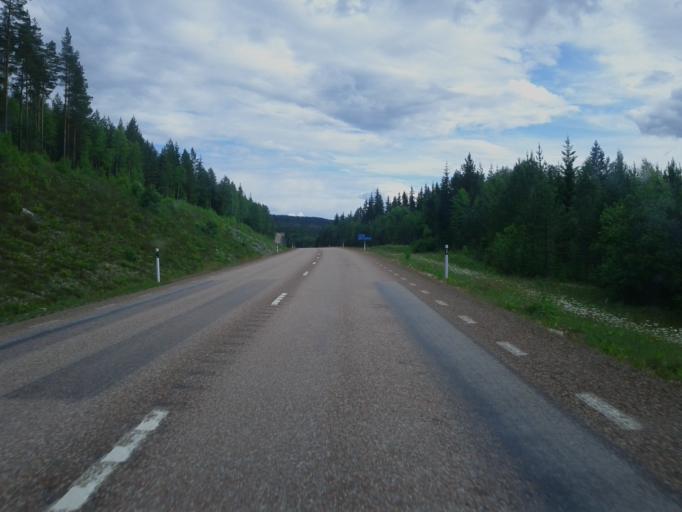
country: SE
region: Dalarna
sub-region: Rattviks Kommun
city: Raettvik
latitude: 60.7970
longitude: 15.2718
